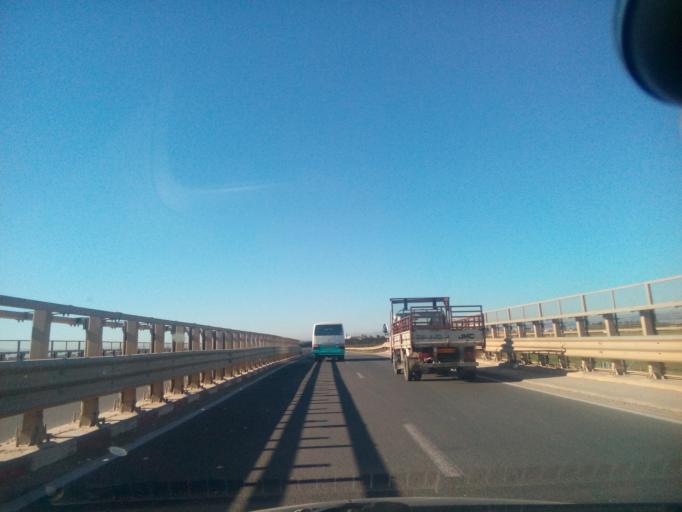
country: DZ
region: Relizane
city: Djidiouia
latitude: 35.8969
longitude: 0.7114
